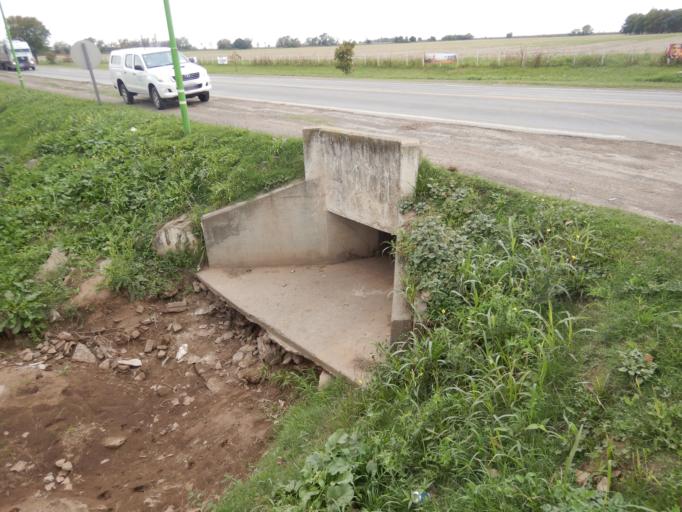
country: AR
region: Santa Fe
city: Carcarana
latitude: -32.8653
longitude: -61.1342
